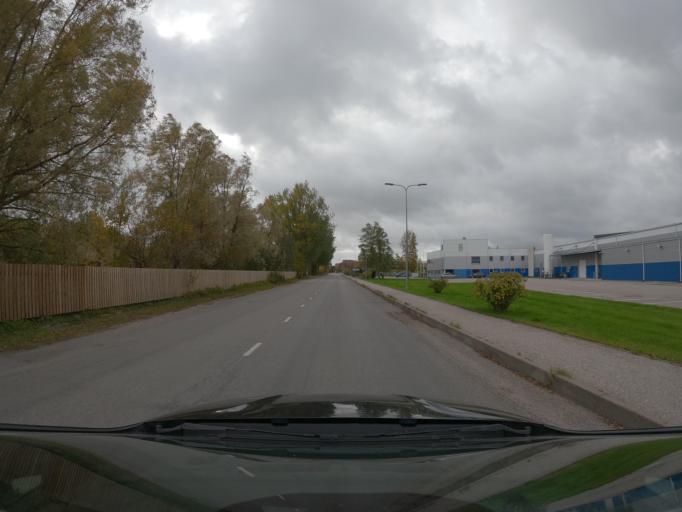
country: EE
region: Saare
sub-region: Kuressaare linn
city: Kuressaare
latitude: 58.2660
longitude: 22.4932
